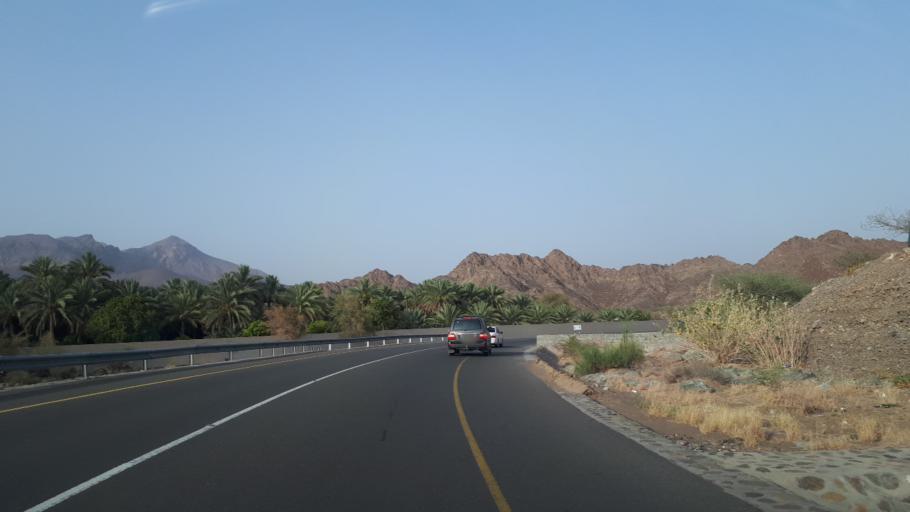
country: OM
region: Az Zahirah
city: Yanqul
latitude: 23.4988
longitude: 56.8329
